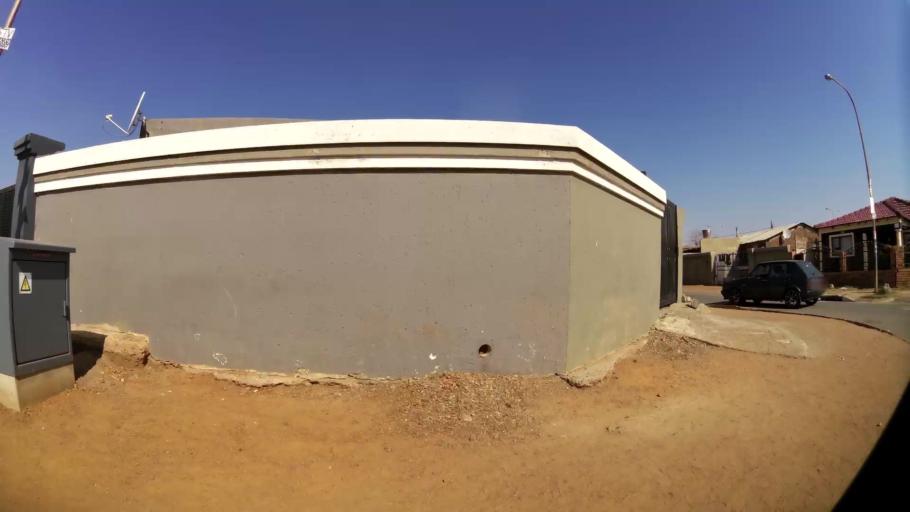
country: ZA
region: Gauteng
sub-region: City of Johannesburg Metropolitan Municipality
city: Soweto
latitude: -26.2413
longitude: 27.9508
